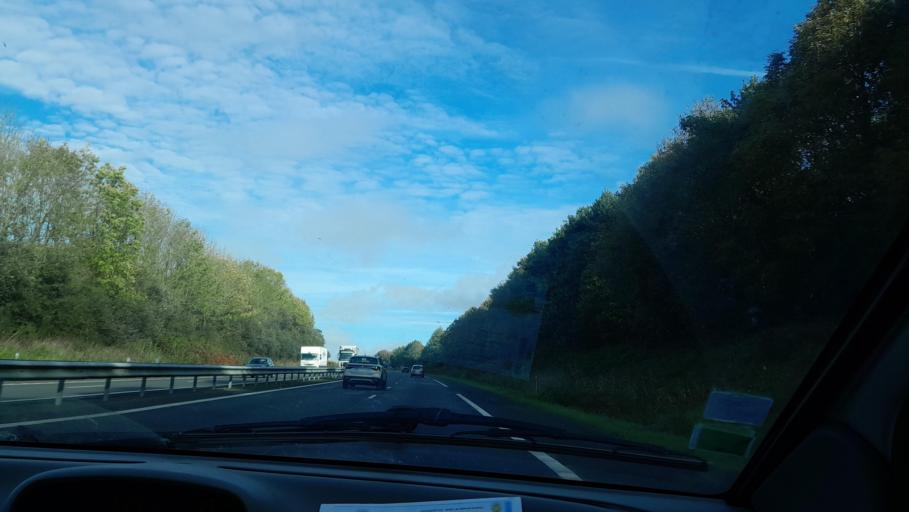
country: FR
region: Brittany
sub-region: Departement d'Ille-et-Vilaine
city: Saint-Etienne-en-Cogles
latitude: 48.4137
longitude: -1.3117
